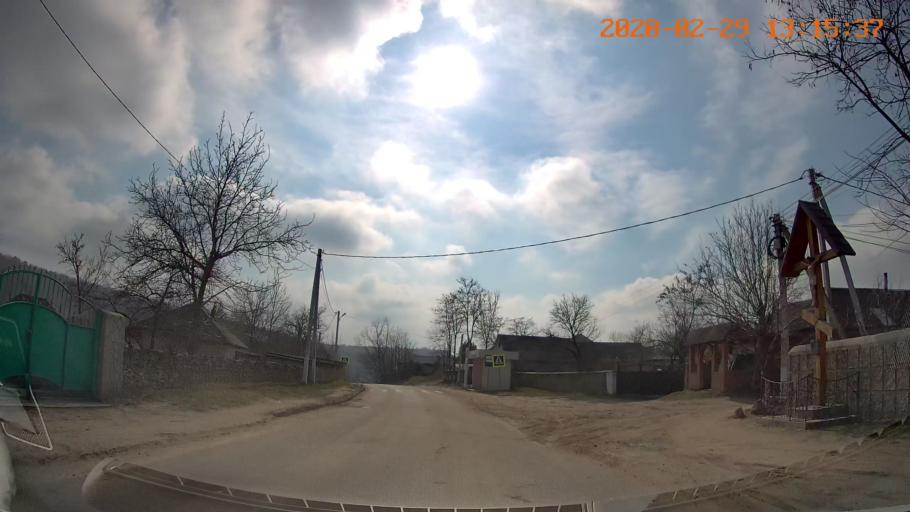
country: MD
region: Telenesti
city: Camenca
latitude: 48.0087
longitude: 28.6683
